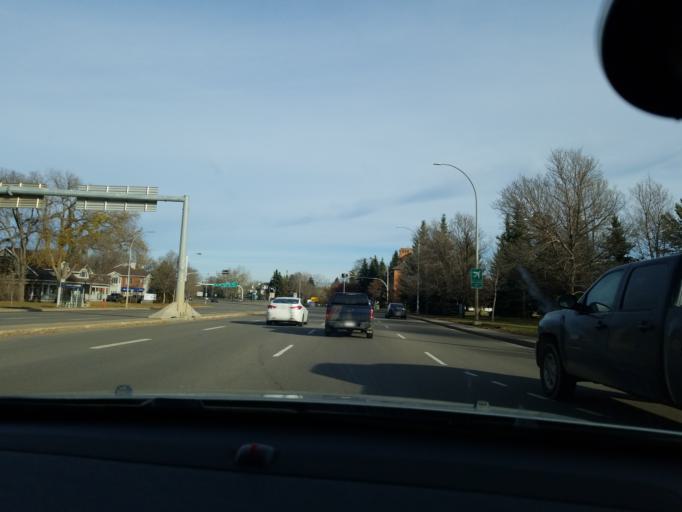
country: CA
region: Alberta
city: Edmonton
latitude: 53.5339
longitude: -113.4969
